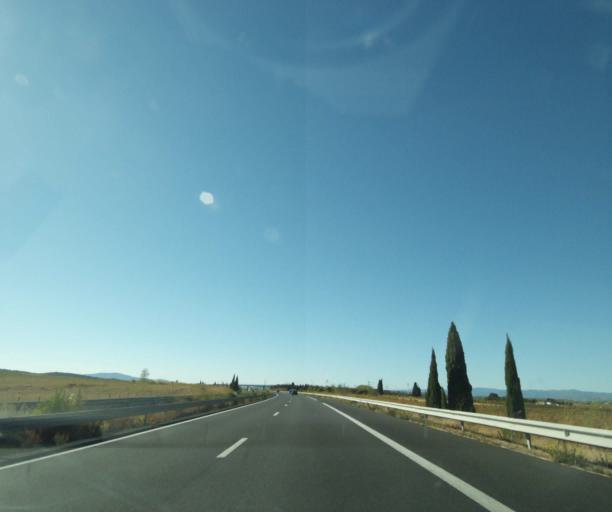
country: FR
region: Languedoc-Roussillon
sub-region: Departement de l'Aude
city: Ornaisons
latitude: 43.1669
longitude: 2.8370
